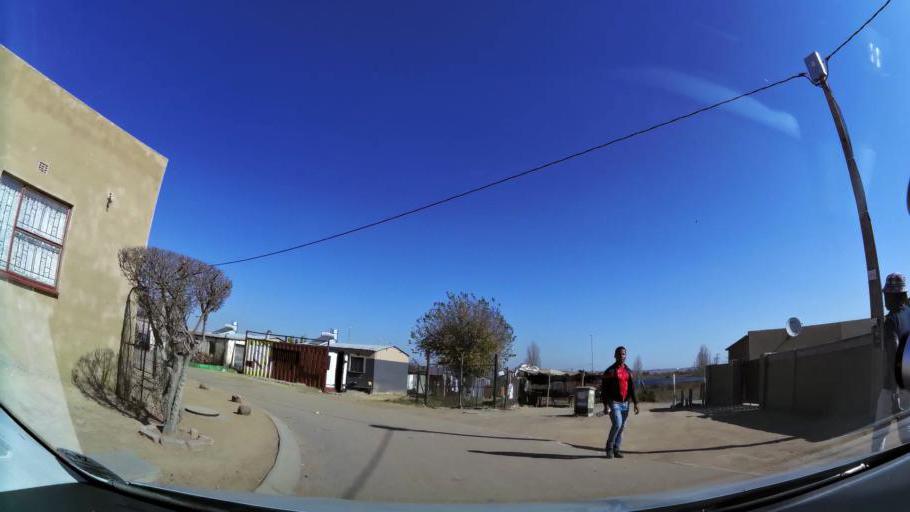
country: ZA
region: Gauteng
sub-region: Ekurhuleni Metropolitan Municipality
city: Tembisa
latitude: -26.0261
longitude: 28.2329
